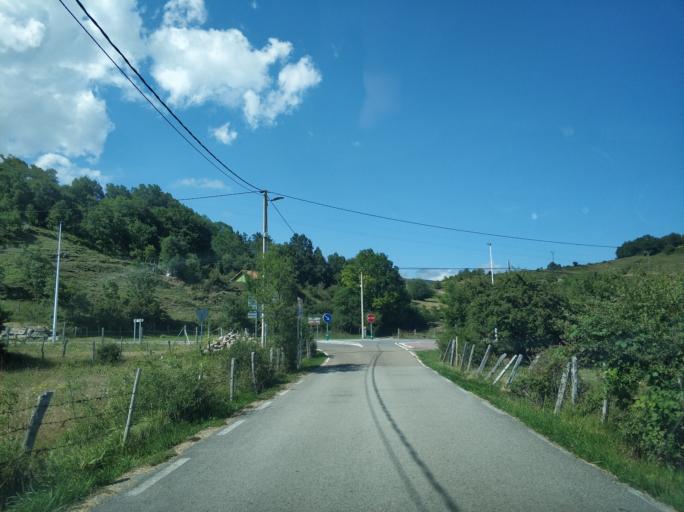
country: ES
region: Castille and Leon
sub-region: Provincia de Palencia
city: Branosera
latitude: 43.0190
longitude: -4.2513
